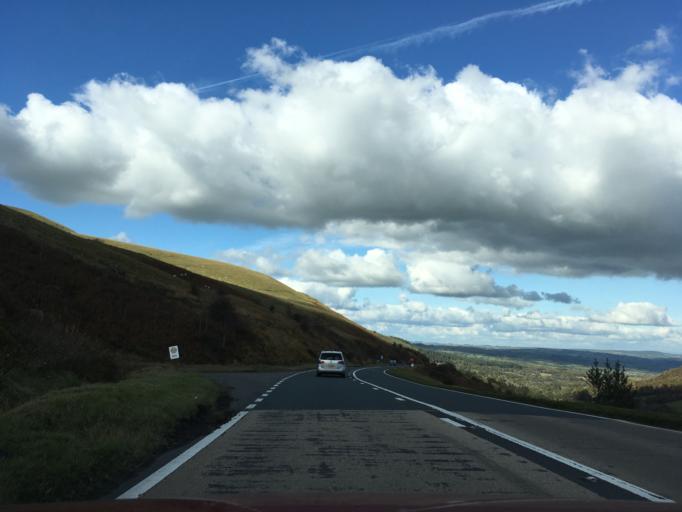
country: GB
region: Wales
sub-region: Sir Powys
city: Cray
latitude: 51.8779
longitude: -3.4948
